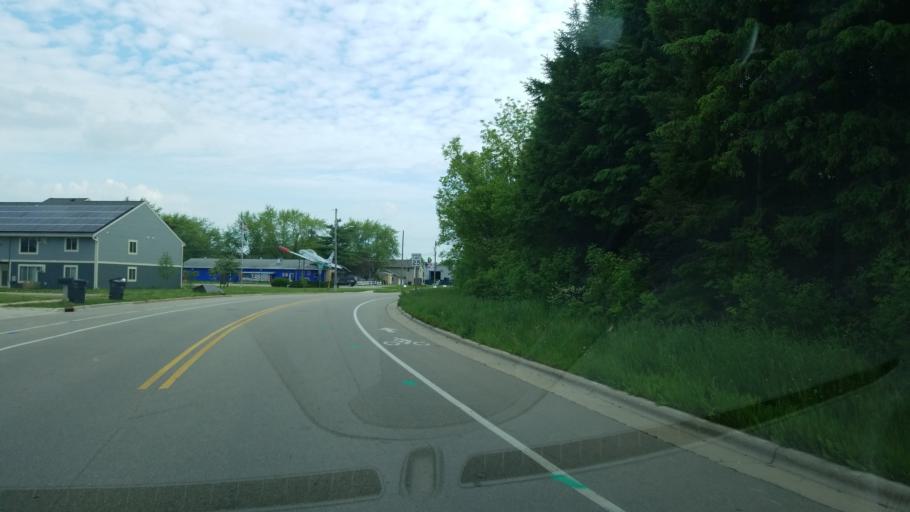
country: US
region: Wisconsin
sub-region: Dane County
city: Stoughton
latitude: 42.9159
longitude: -89.2004
